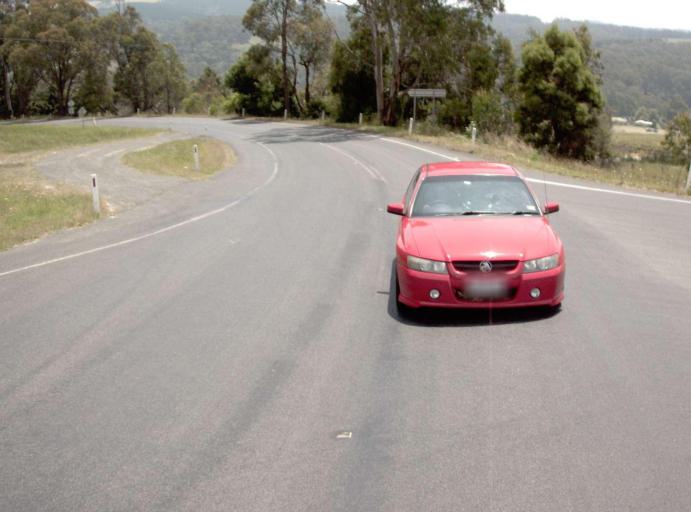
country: AU
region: Victoria
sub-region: Latrobe
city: Traralgon
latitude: -38.3813
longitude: 146.7590
